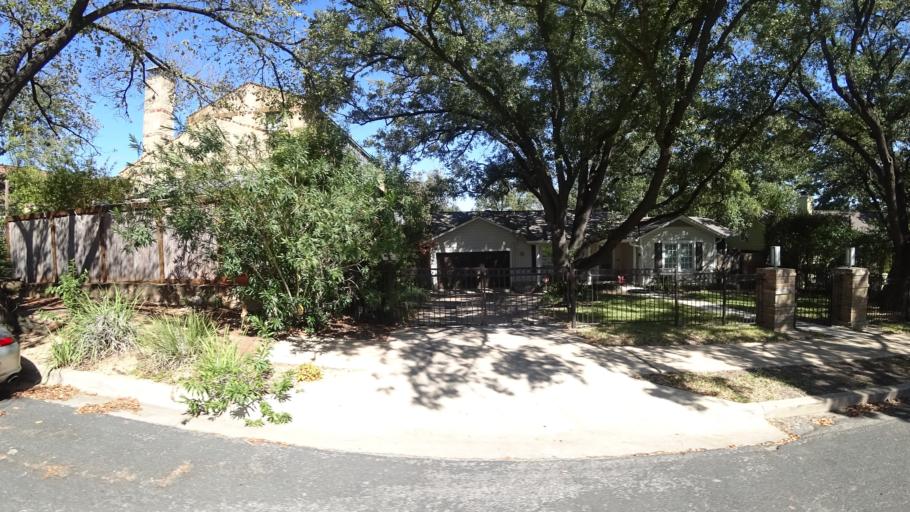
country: US
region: Texas
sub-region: Travis County
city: Rollingwood
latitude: 30.2965
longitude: -97.7625
